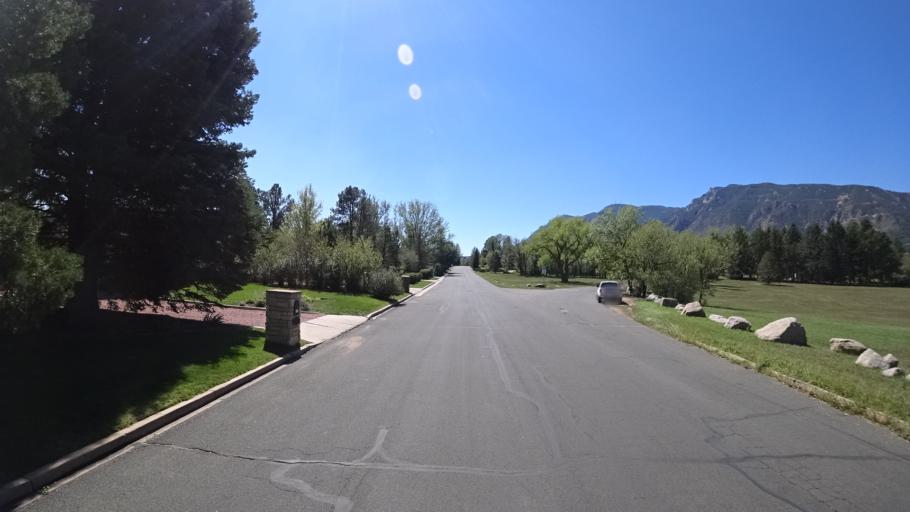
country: US
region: Colorado
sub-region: El Paso County
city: Colorado Springs
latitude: 38.7859
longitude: -104.8374
